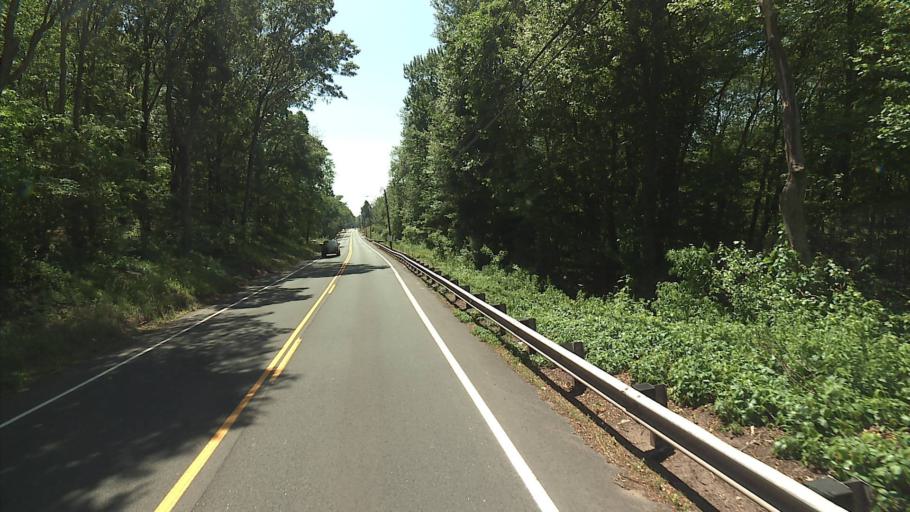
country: US
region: Connecticut
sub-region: Tolland County
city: Rockville
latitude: 41.8521
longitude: -72.4464
